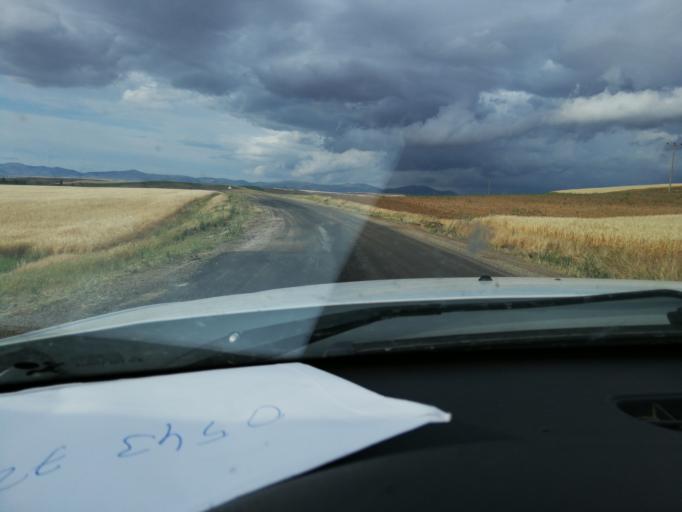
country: TR
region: Kirsehir
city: Kirsehir
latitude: 39.0331
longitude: 34.1413
